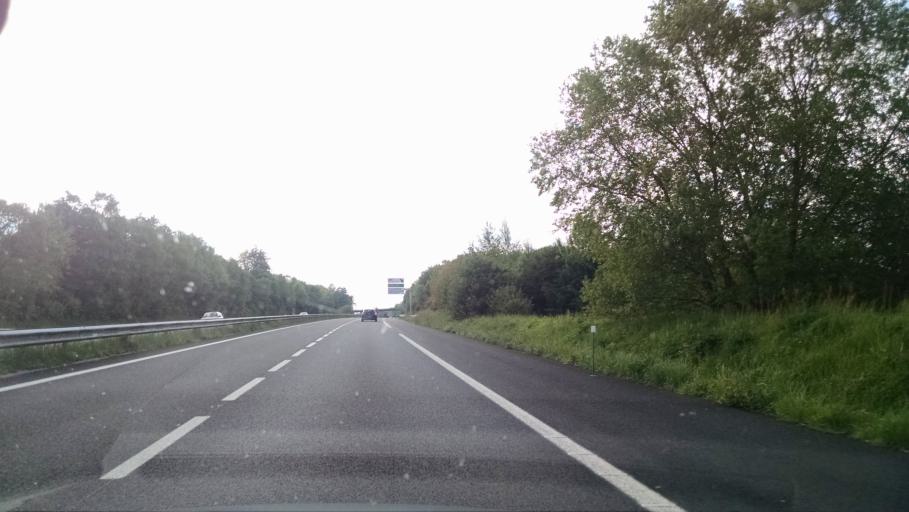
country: FR
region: Brittany
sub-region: Departement des Cotes-d'Armor
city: Plounevez-Moedec
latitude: 48.5595
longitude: -3.4942
